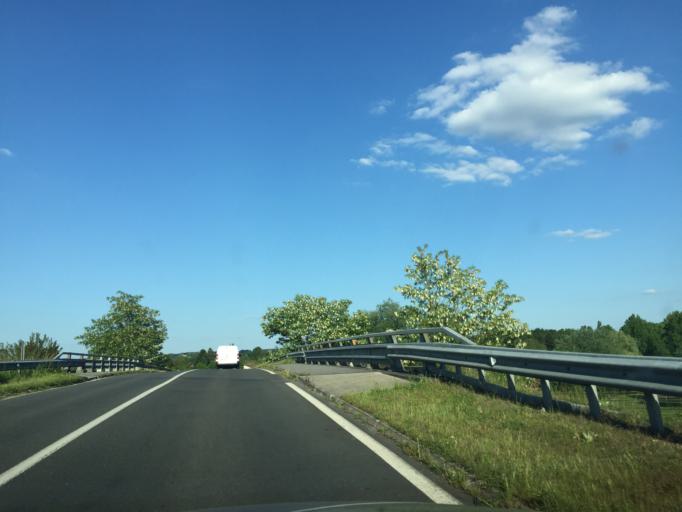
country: FR
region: Aquitaine
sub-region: Departement de la Gironde
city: Les Eglisottes-et-Chalaures
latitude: 45.0897
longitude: -0.0514
